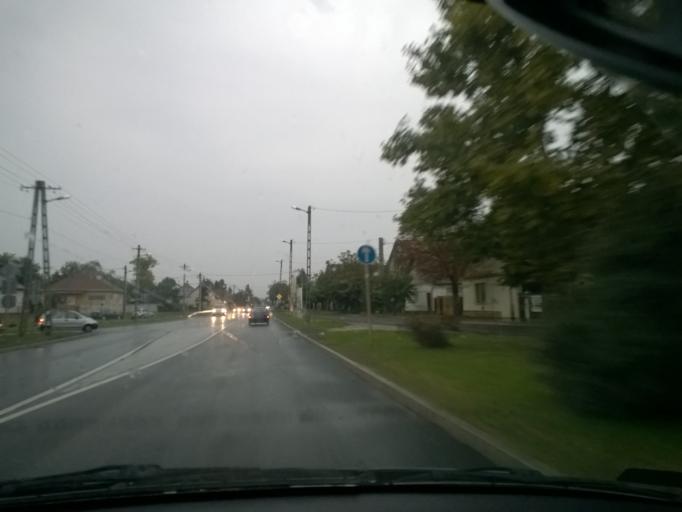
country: HU
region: Pest
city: Kiskunlachaza
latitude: 47.1771
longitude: 19.0008
